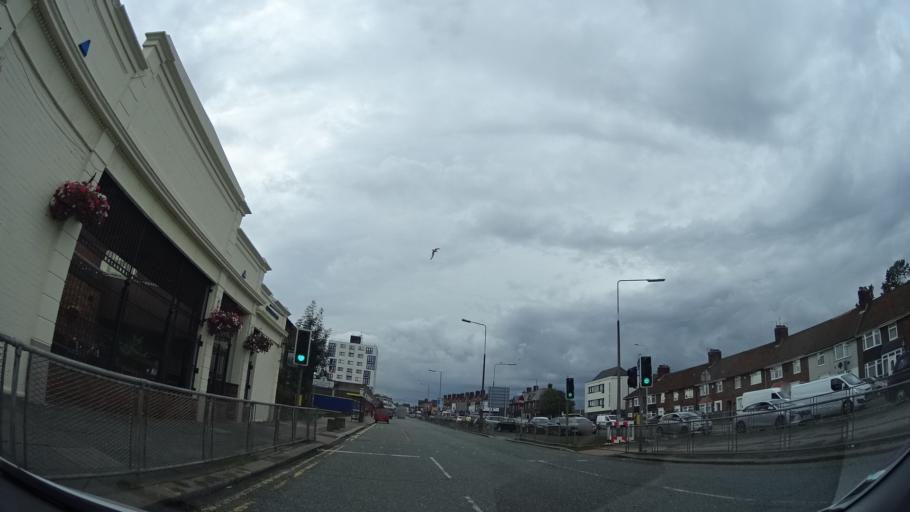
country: GB
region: England
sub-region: Knowsley
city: Knowsley
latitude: 53.4152
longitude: -2.9058
